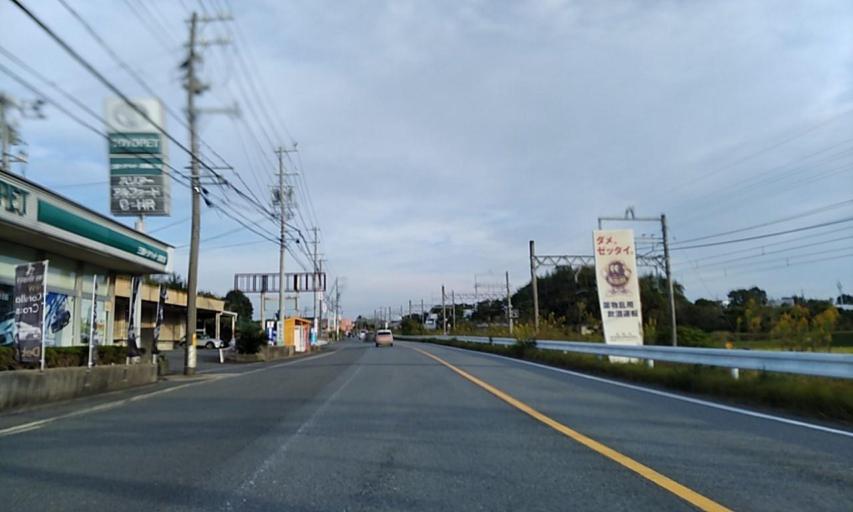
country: JP
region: Mie
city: Toba
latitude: 34.3413
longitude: 136.8165
